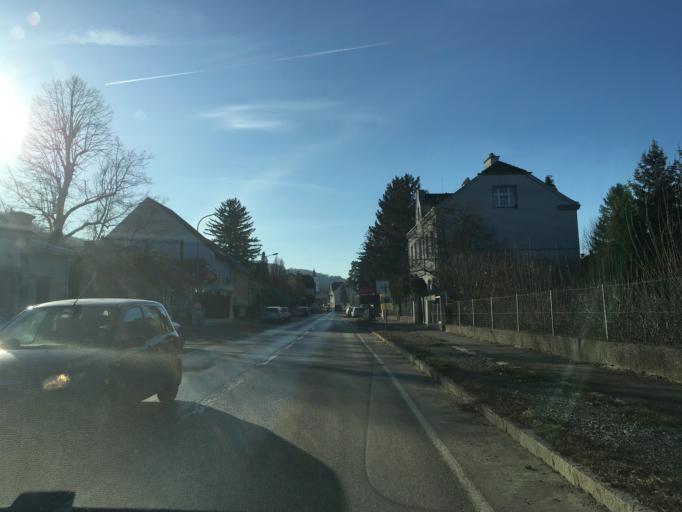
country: AT
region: Lower Austria
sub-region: Politischer Bezirk Tulln
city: Wordern
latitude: 48.3249
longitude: 16.2133
